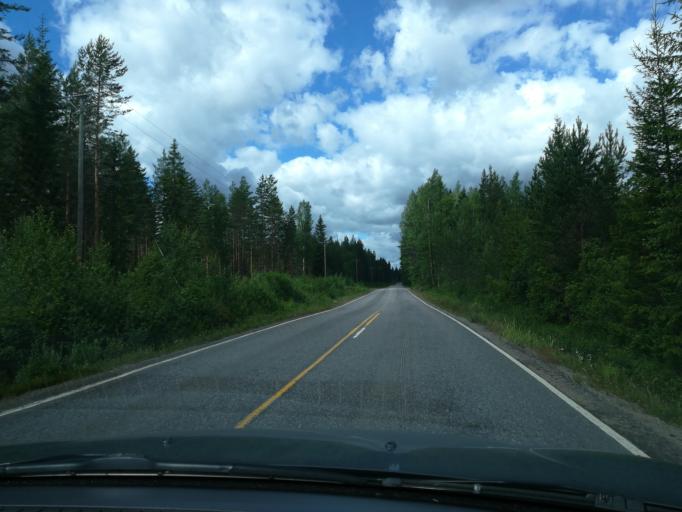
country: FI
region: Southern Savonia
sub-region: Mikkeli
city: Ristiina
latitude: 61.3571
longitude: 27.0999
